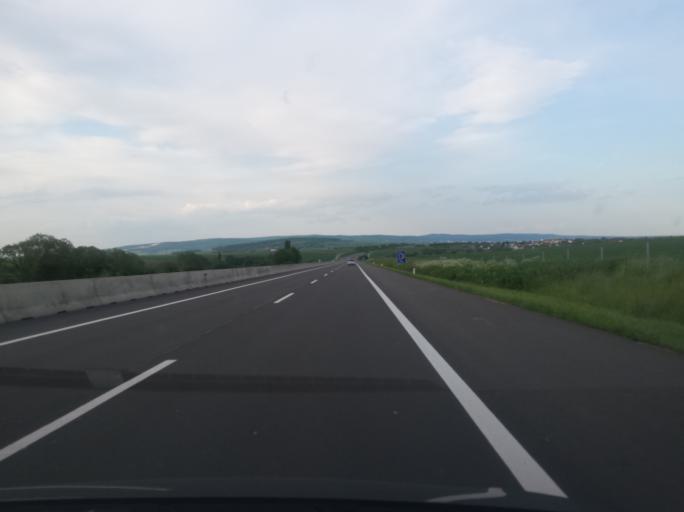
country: AT
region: Burgenland
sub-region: Politischer Bezirk Mattersburg
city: Hirm
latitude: 47.7807
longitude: 16.4366
